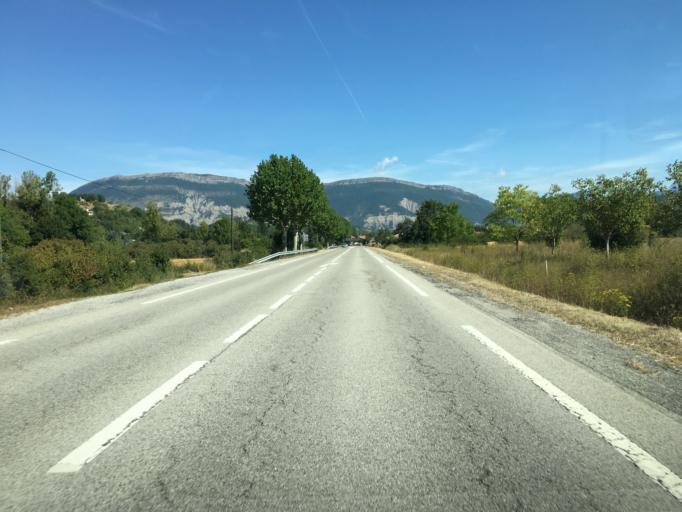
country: FR
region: Provence-Alpes-Cote d'Azur
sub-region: Departement des Hautes-Alpes
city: Serres
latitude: 44.4849
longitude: 5.7287
